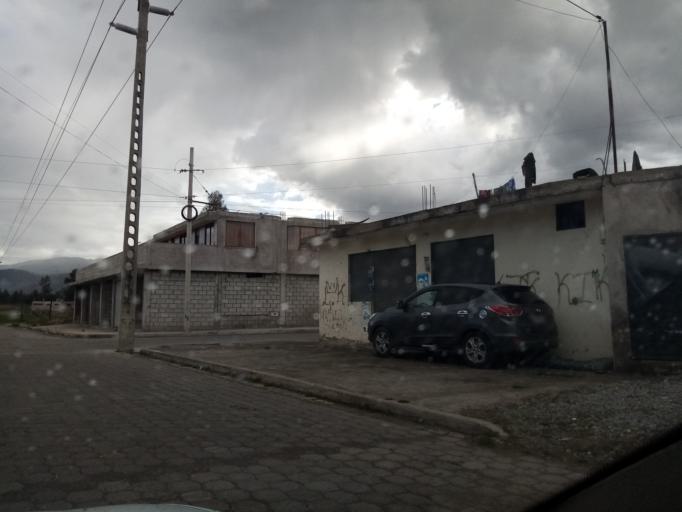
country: EC
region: Chimborazo
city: Riobamba
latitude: -1.6911
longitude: -78.6330
